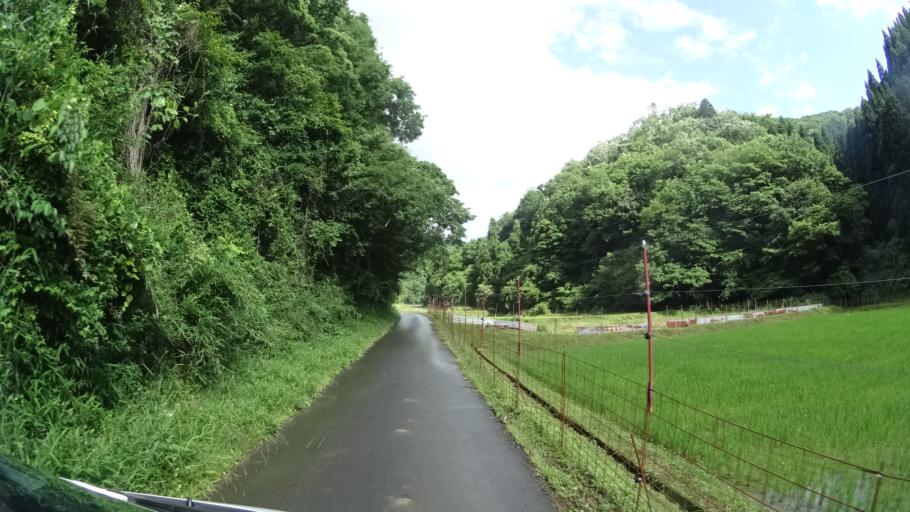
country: JP
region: Kyoto
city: Maizuru
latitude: 35.3932
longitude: 135.2669
